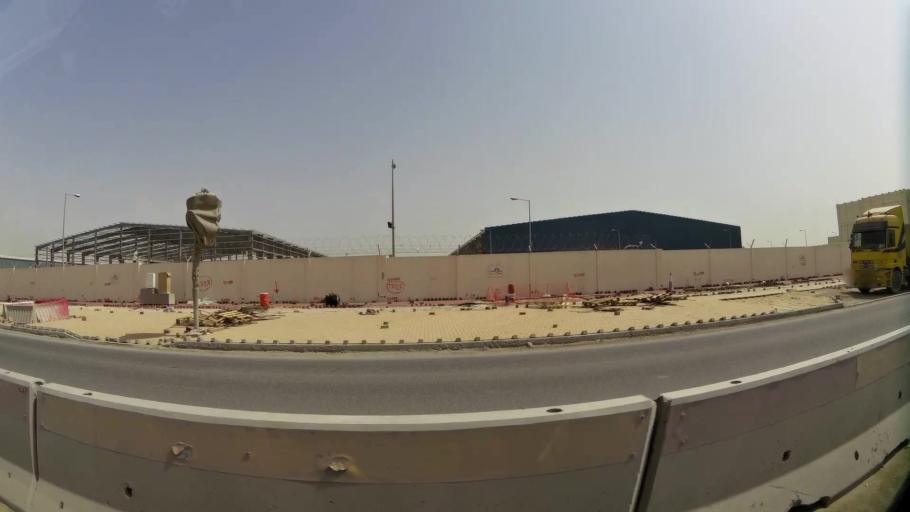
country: QA
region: Baladiyat ar Rayyan
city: Ar Rayyan
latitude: 25.2014
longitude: 51.4129
